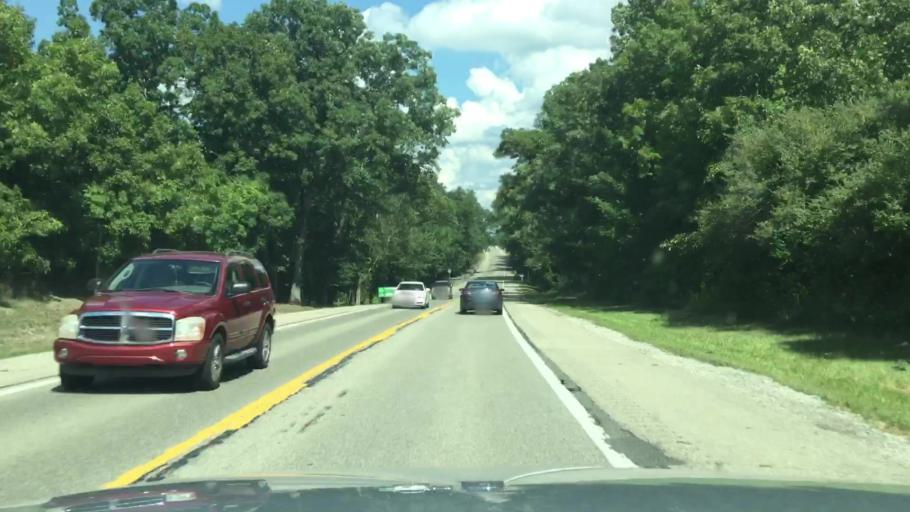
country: US
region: Michigan
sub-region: Lenawee County
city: Clinton
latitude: 42.1121
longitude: -83.8860
